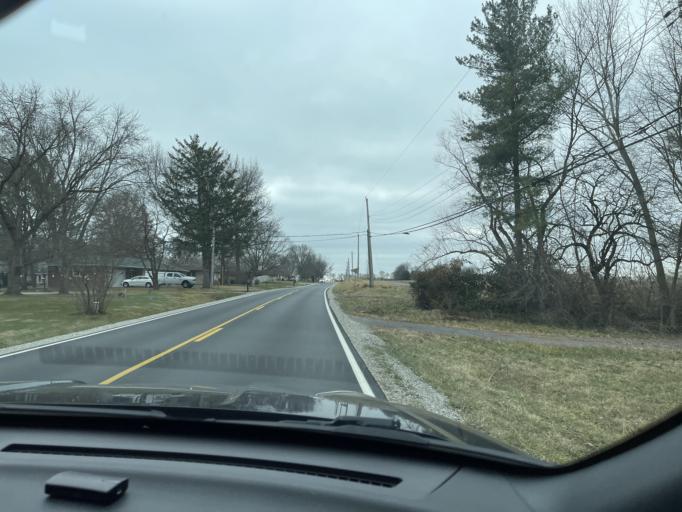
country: US
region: Illinois
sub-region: Sangamon County
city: Leland Grove
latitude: 39.7906
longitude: -89.7391
